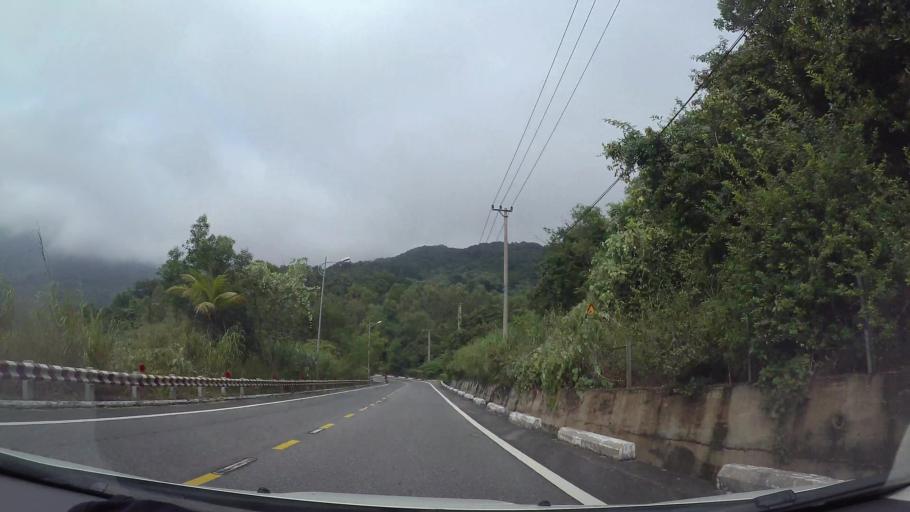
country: VN
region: Da Nang
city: Son Tra
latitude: 16.1013
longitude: 108.3036
